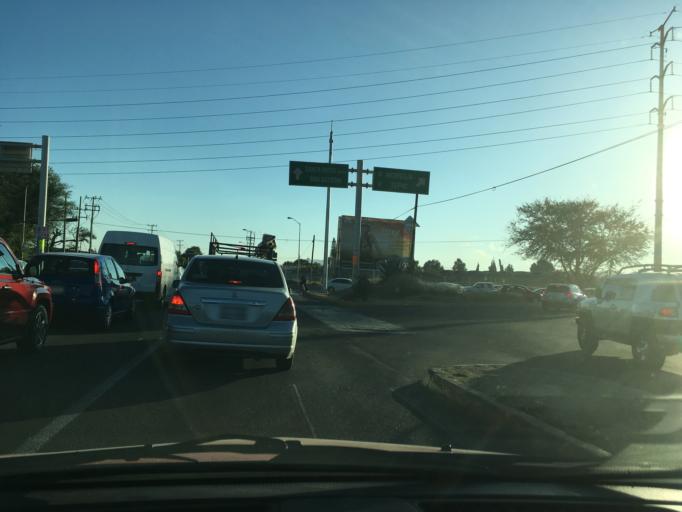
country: MX
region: Jalisco
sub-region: Tlajomulco de Zuniga
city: La Tijera
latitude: 20.5716
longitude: -103.4385
